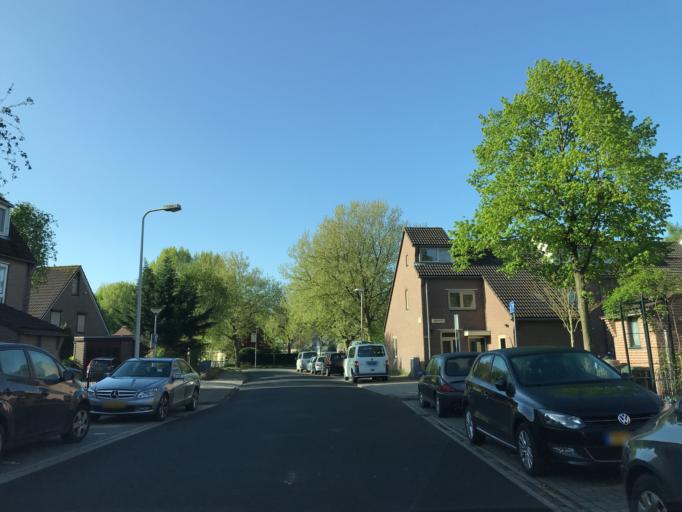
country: NL
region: North Holland
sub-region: Gemeente Diemen
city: Diemen
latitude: 52.3351
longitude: 4.9621
